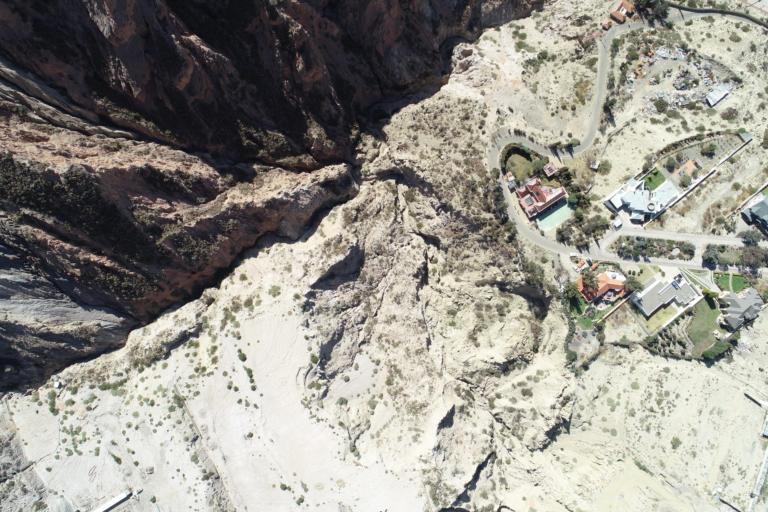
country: BO
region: La Paz
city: La Paz
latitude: -16.5564
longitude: -68.1050
